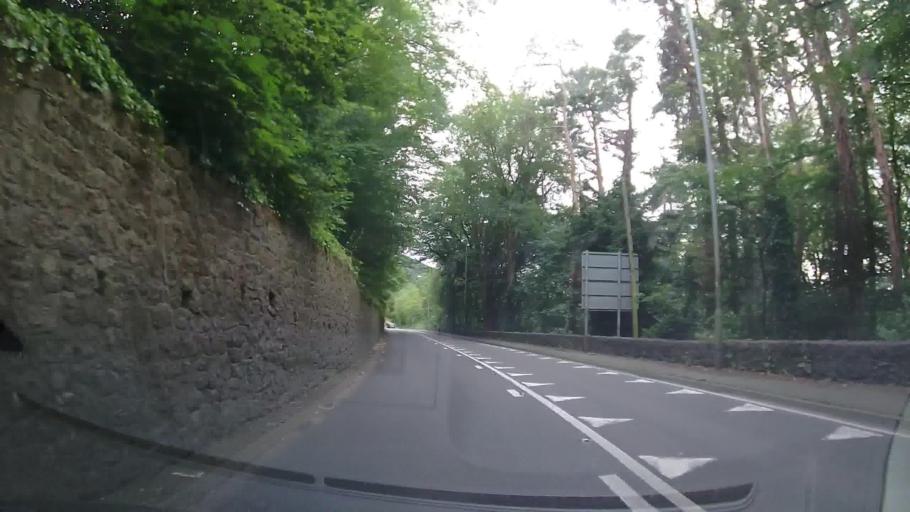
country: GB
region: Wales
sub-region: Wrexham
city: Chirk
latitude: 52.9640
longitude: -3.0895
